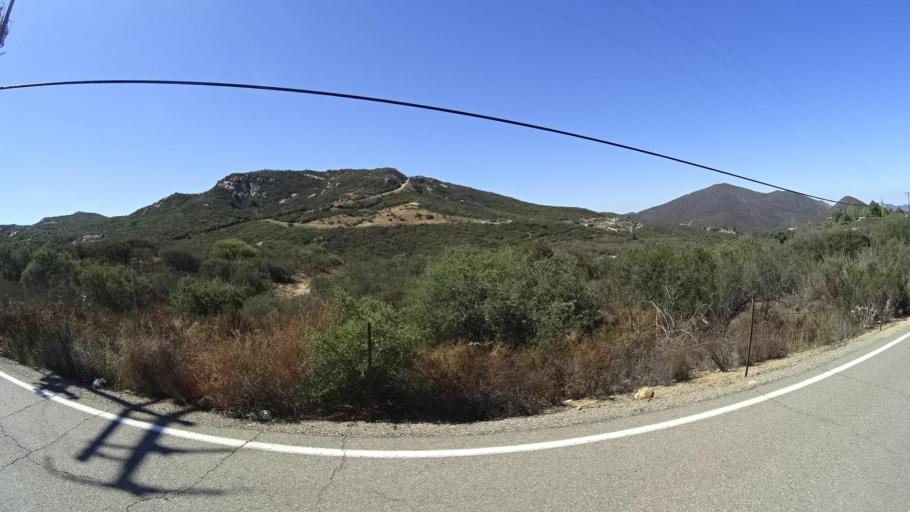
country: US
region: California
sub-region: San Diego County
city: Alpine
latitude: 32.7538
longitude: -116.7624
